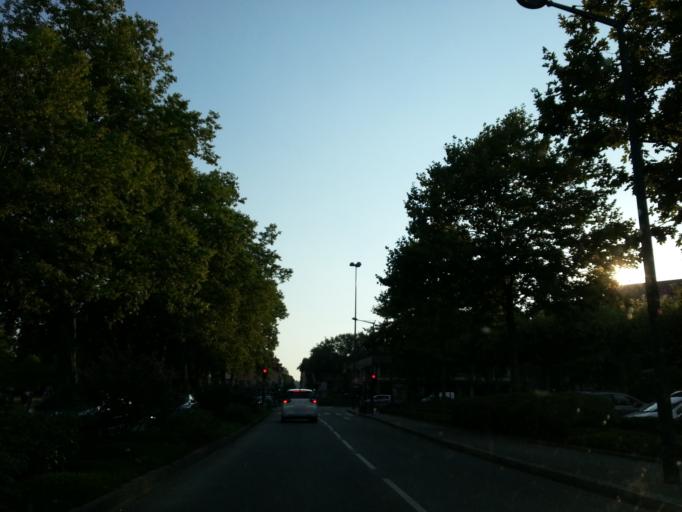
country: FR
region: Rhone-Alpes
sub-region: Departement de la Haute-Savoie
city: Annecy
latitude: 45.9019
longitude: 6.1299
